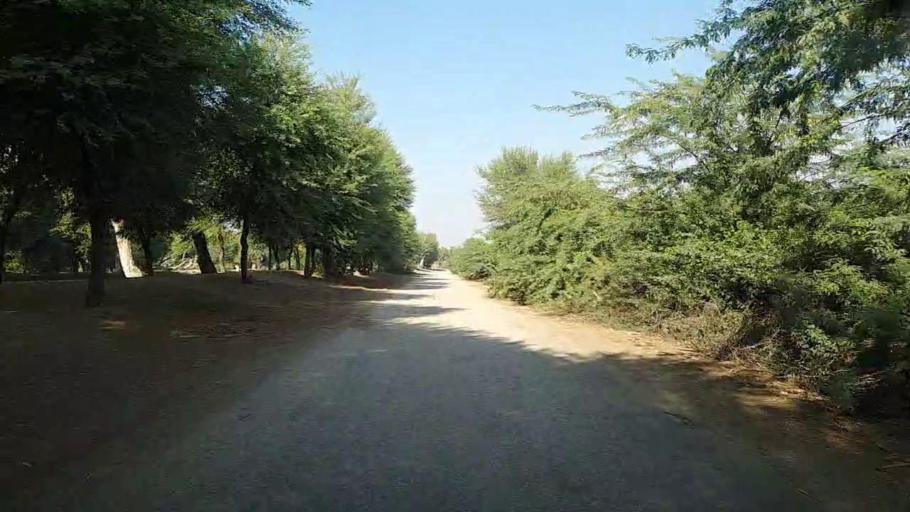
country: PK
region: Sindh
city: Bozdar
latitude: 27.1962
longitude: 68.6655
